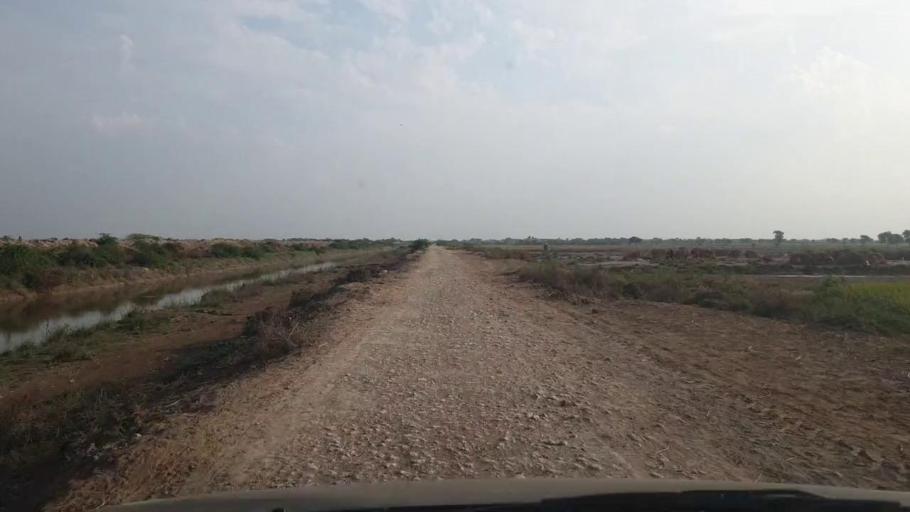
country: PK
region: Sindh
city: Badin
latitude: 24.5587
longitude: 68.6690
